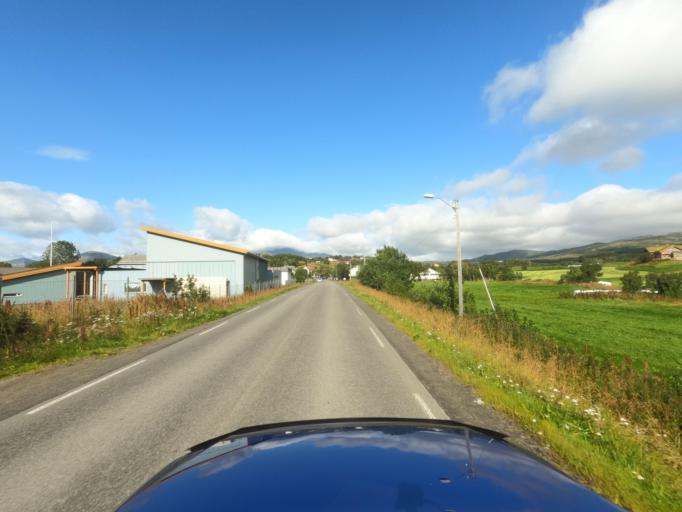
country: NO
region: Nordland
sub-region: Vestvagoy
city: Leknes
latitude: 68.1434
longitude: 13.6508
